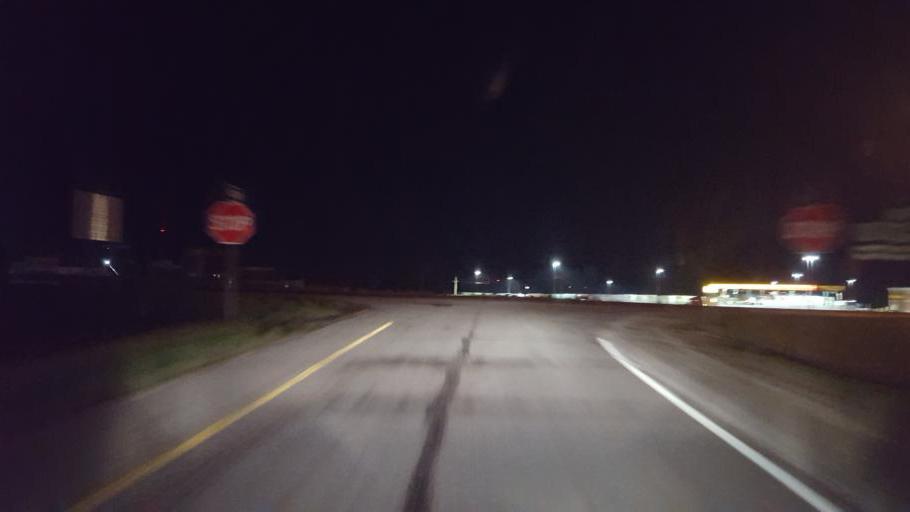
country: US
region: Iowa
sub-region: Decatur County
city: Lamoni
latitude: 40.4670
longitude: -93.9778
